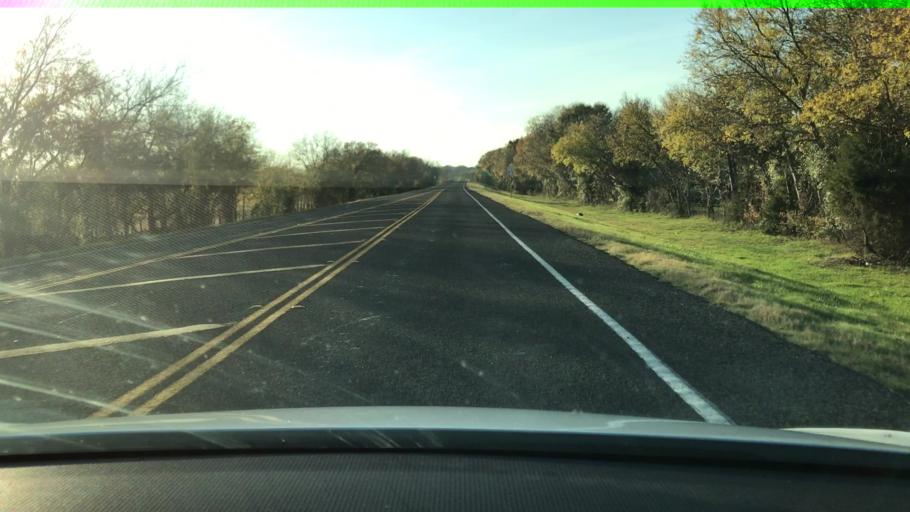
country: US
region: Texas
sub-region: Kaufman County
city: Kemp
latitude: 32.5701
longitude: -96.1299
